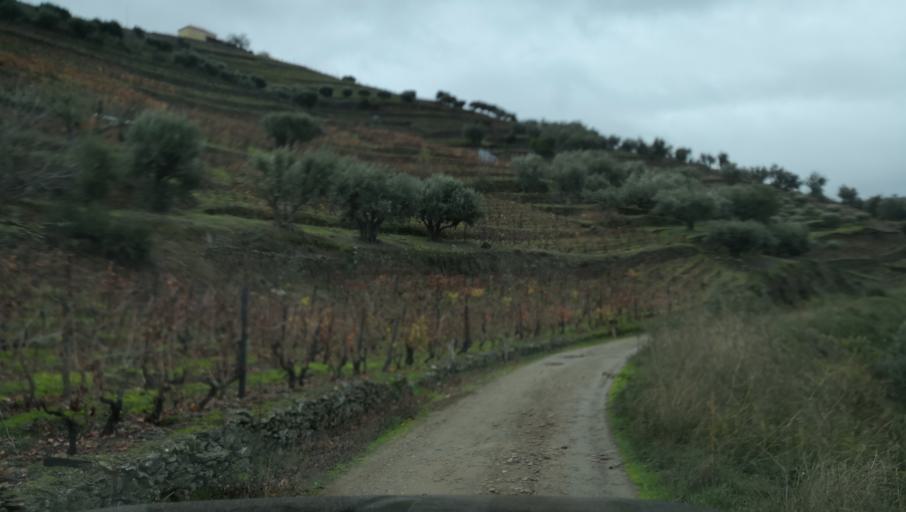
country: PT
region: Vila Real
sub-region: Vila Real
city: Vila Real
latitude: 41.2425
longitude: -7.7494
